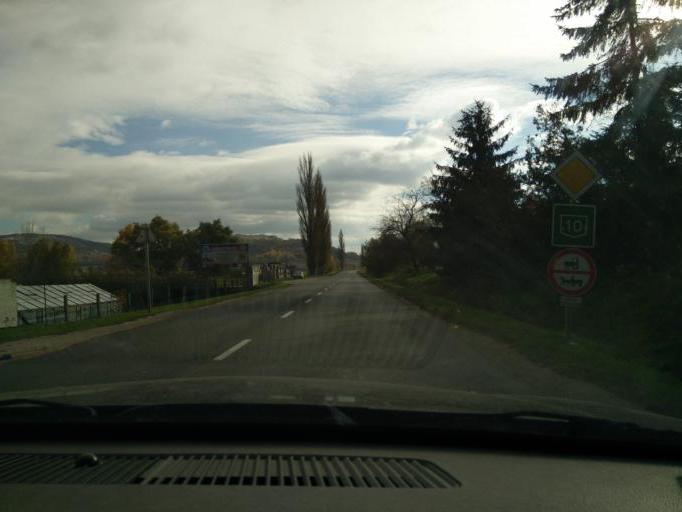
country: HU
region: Komarom-Esztergom
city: Piliscsev
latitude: 47.6777
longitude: 18.7777
